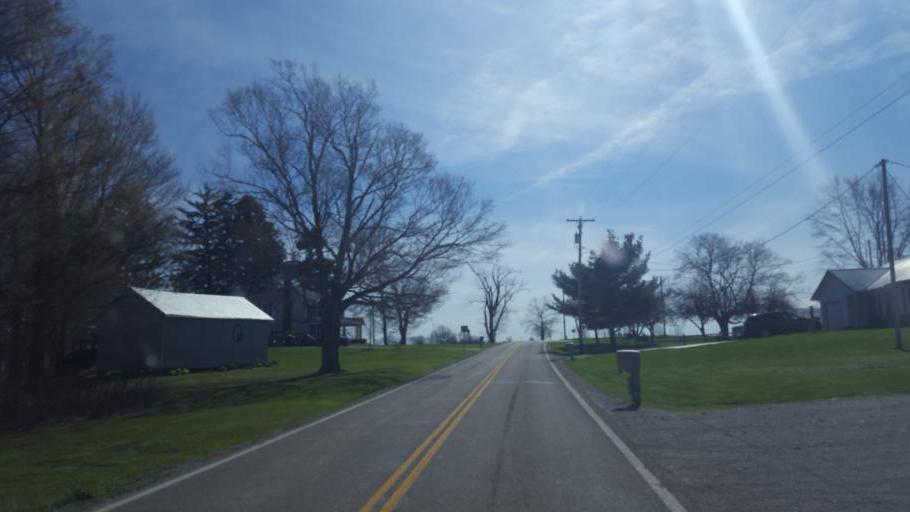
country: US
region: Ohio
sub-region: Delaware County
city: Ashley
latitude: 40.4547
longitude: -82.9571
